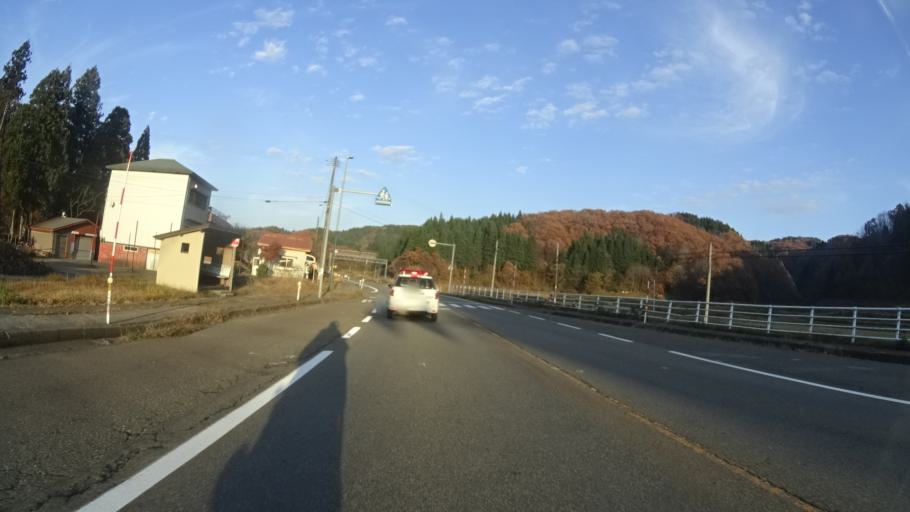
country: JP
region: Niigata
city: Nagaoka
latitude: 37.4202
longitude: 138.7223
